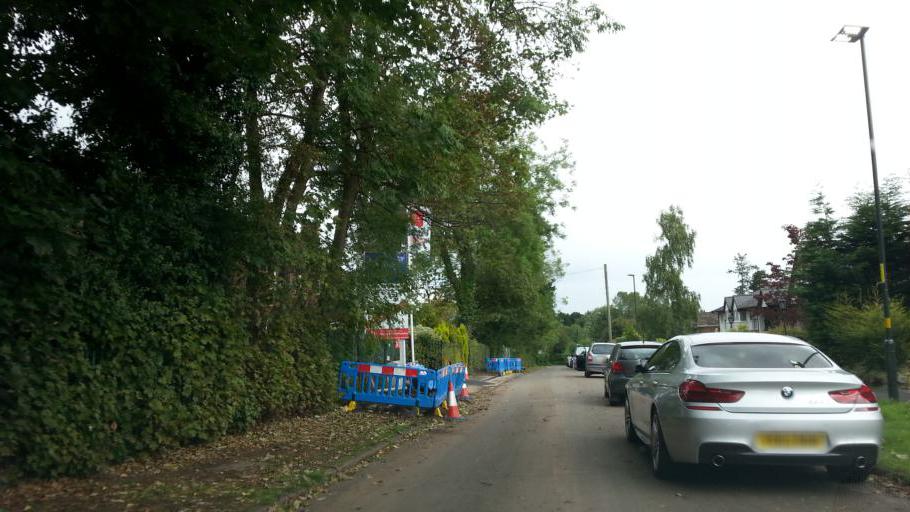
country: GB
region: England
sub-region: City and Borough of Birmingham
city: Birmingham
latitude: 52.4404
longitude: -1.9175
